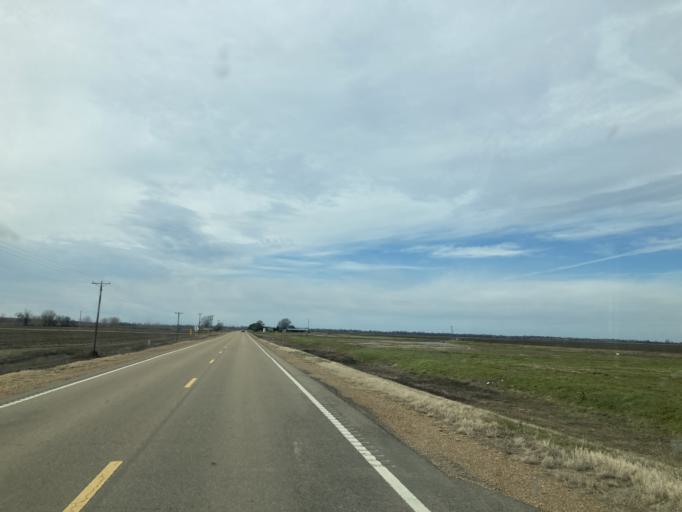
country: US
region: Mississippi
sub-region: Humphreys County
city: Belzoni
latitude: 33.1826
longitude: -90.6335
